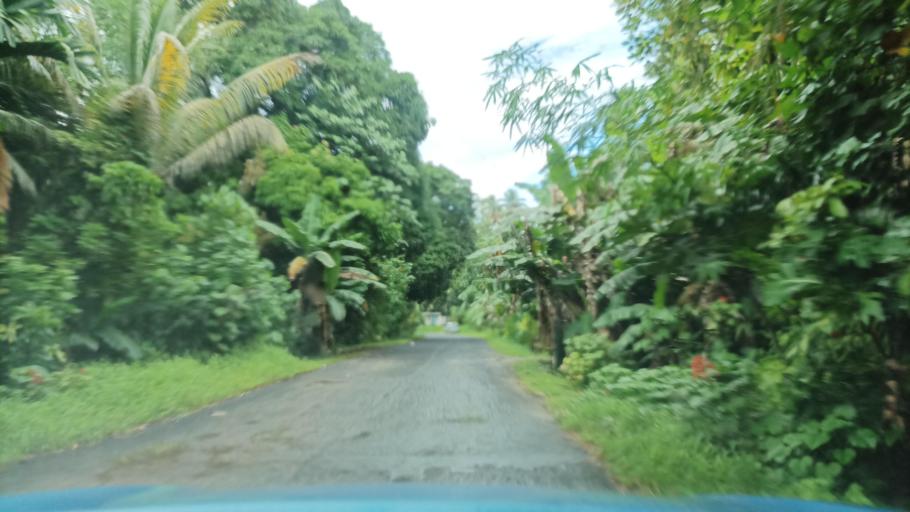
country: FM
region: Pohnpei
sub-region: Sokehs Municipality
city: Palikir - National Government Center
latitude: 6.8219
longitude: 158.1577
